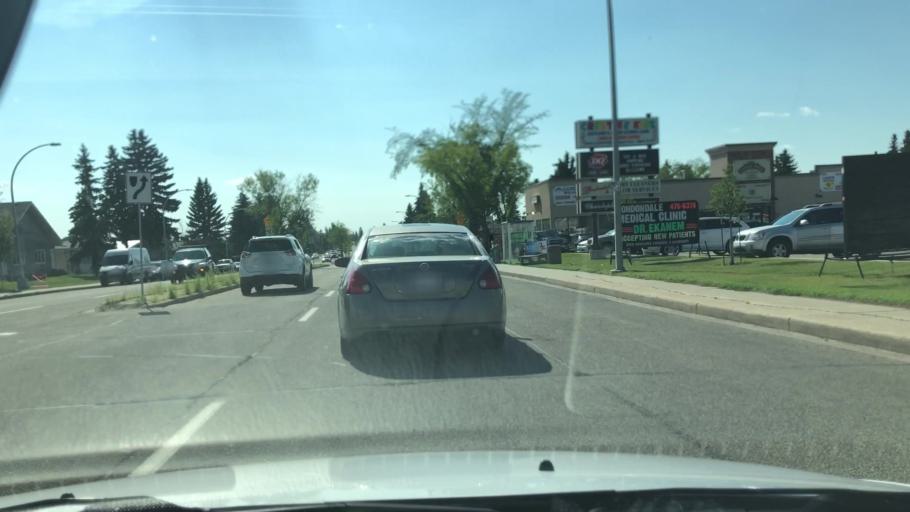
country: CA
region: Alberta
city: Edmonton
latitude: 53.6070
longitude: -113.4588
